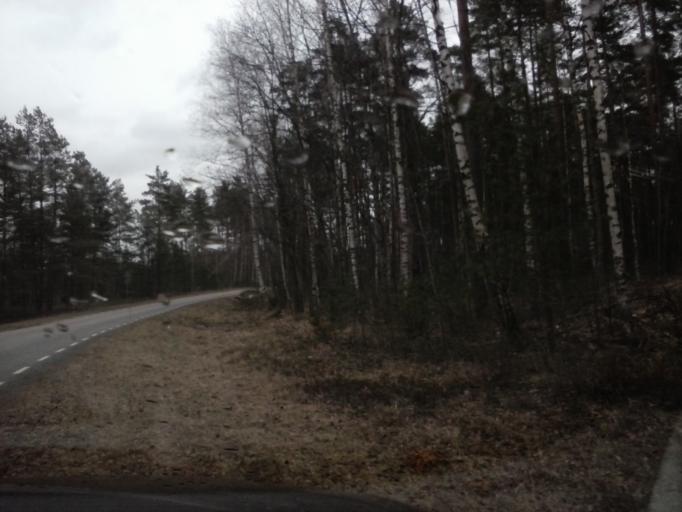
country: RU
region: Pskov
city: Pechory
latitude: 57.9630
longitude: 27.6317
